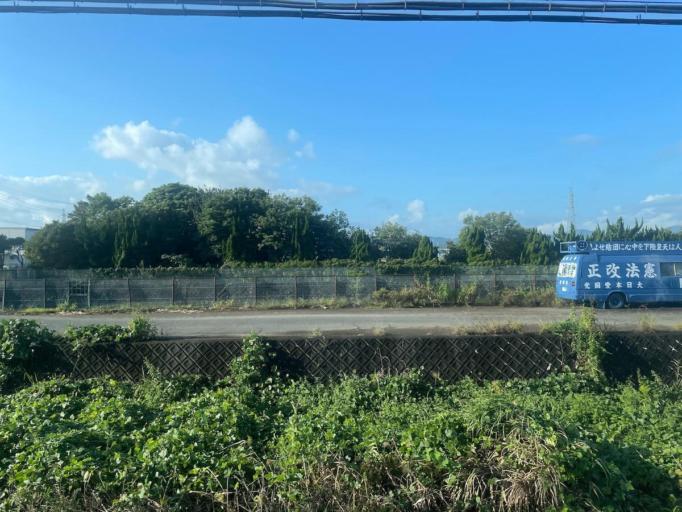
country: JP
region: Mie
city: Hisai-motomachi
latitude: 34.5595
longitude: 136.5586
